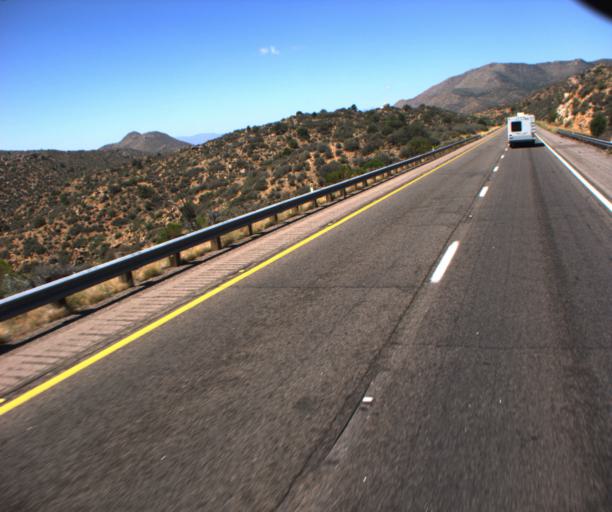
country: US
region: Arizona
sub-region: Mohave County
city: Peach Springs
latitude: 35.1790
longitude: -113.4889
